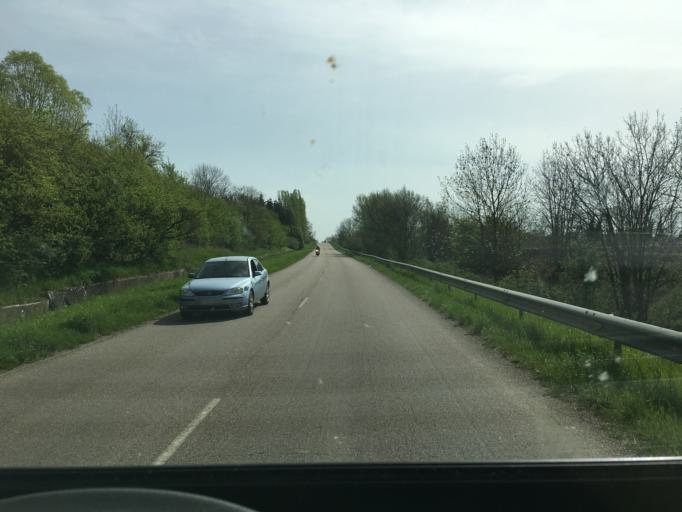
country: FR
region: Lorraine
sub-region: Departement de Meurthe-et-Moselle
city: Messein
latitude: 48.6115
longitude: 6.1287
